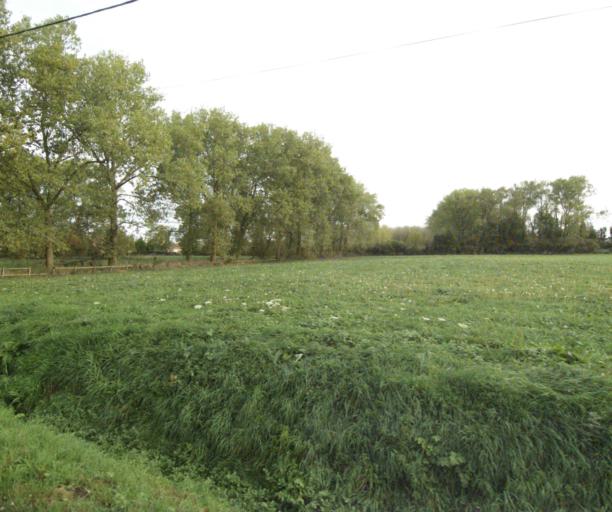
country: FR
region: Nord-Pas-de-Calais
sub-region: Departement du Nord
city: Aubers
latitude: 50.5998
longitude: 2.8286
